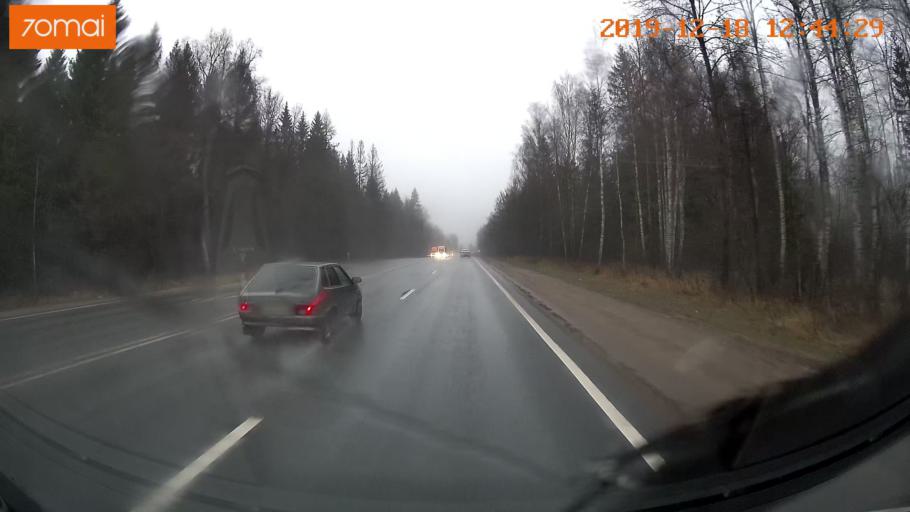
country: RU
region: Moskovskaya
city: Vysokovsk
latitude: 56.2201
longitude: 36.6491
